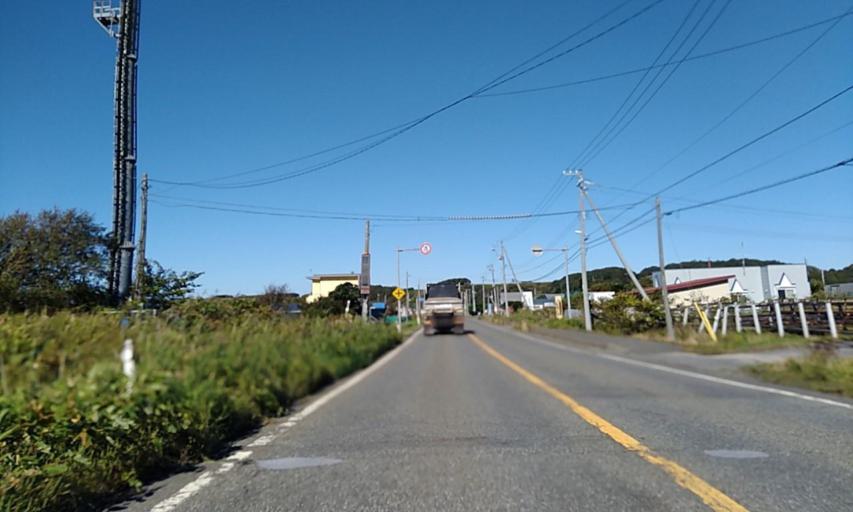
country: JP
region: Hokkaido
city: Shizunai-furukawacho
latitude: 42.4699
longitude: 142.1249
